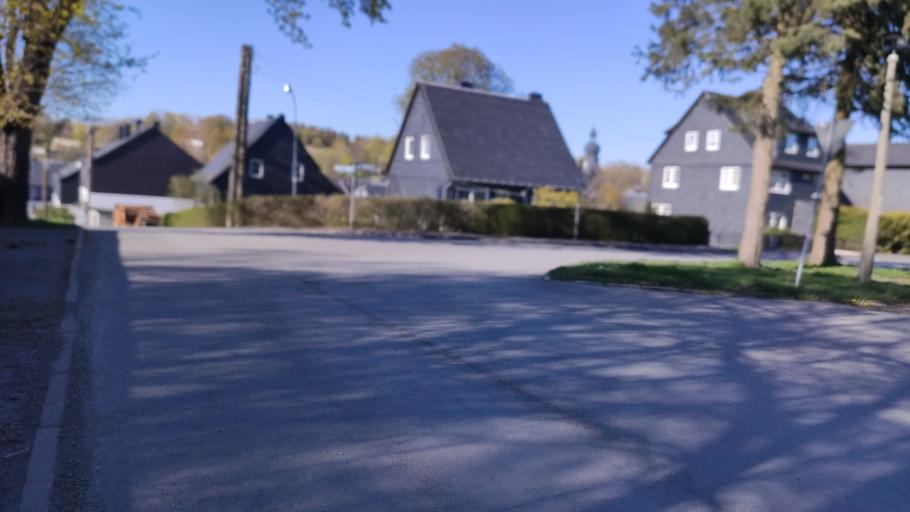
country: DE
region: Bavaria
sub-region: Upper Franconia
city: Ludwigsstadt
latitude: 50.4736
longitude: 11.4465
